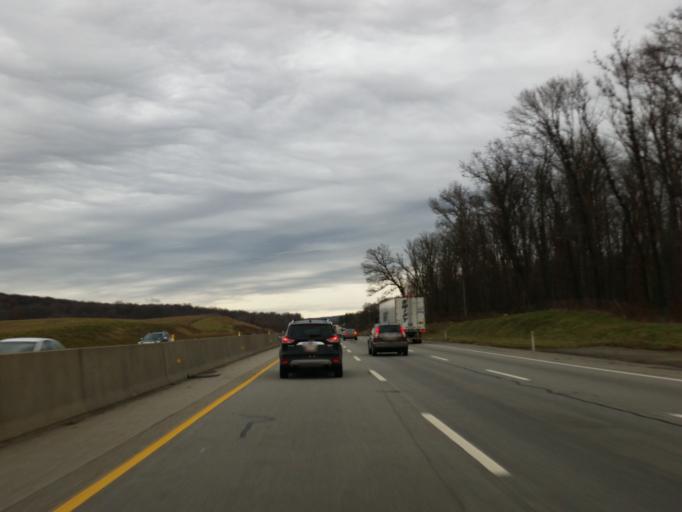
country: US
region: Pennsylvania
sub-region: Fayette County
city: Bear Rocks
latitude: 40.1201
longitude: -79.3287
